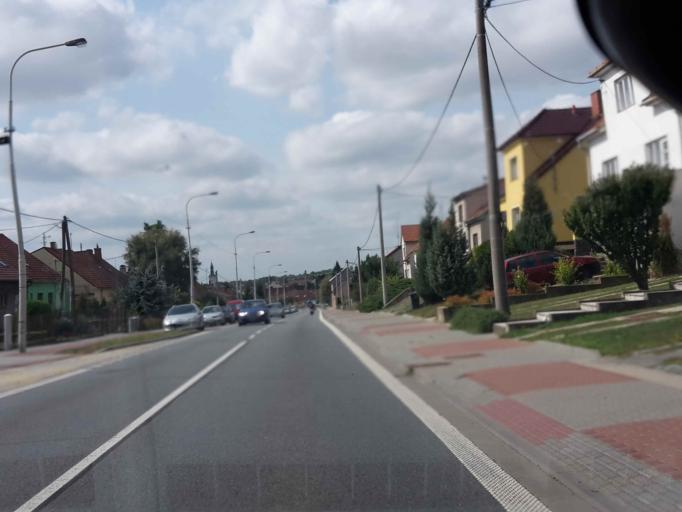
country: CZ
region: South Moravian
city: Rousinov
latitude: 49.2070
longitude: 16.8914
